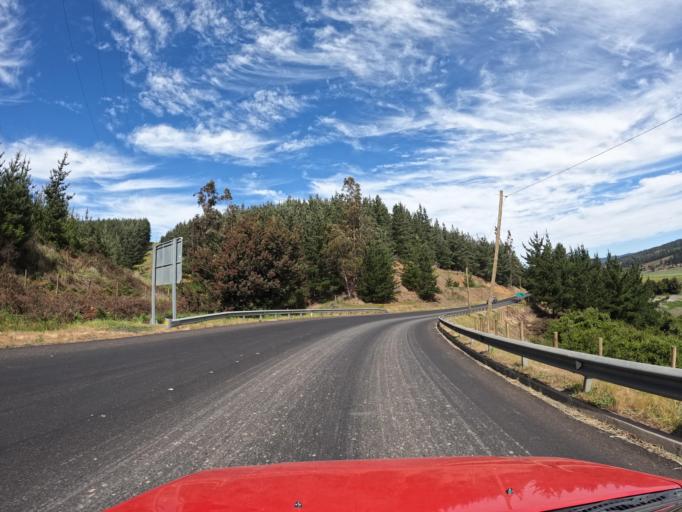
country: CL
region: Maule
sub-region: Provincia de Talca
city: Constitucion
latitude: -35.0414
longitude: -72.0601
